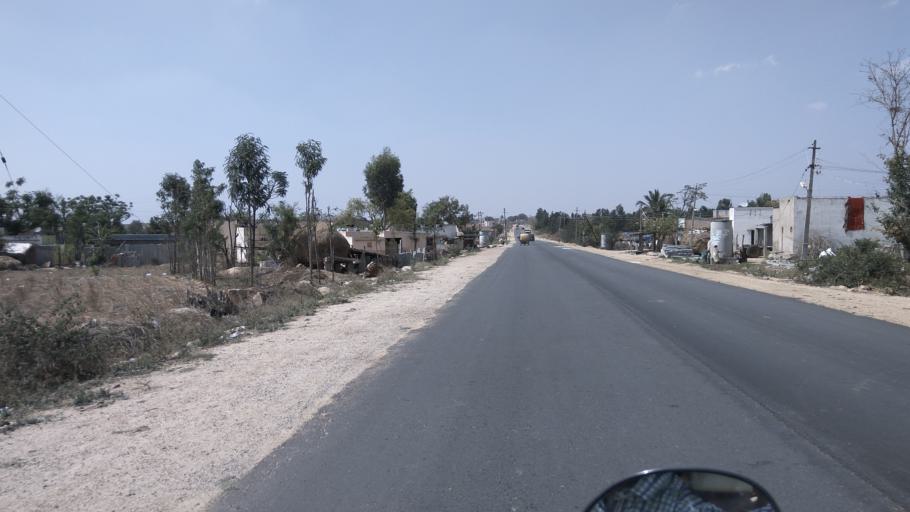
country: IN
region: Karnataka
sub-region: Kolar
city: Mulbagal
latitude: 13.1775
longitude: 78.3533
